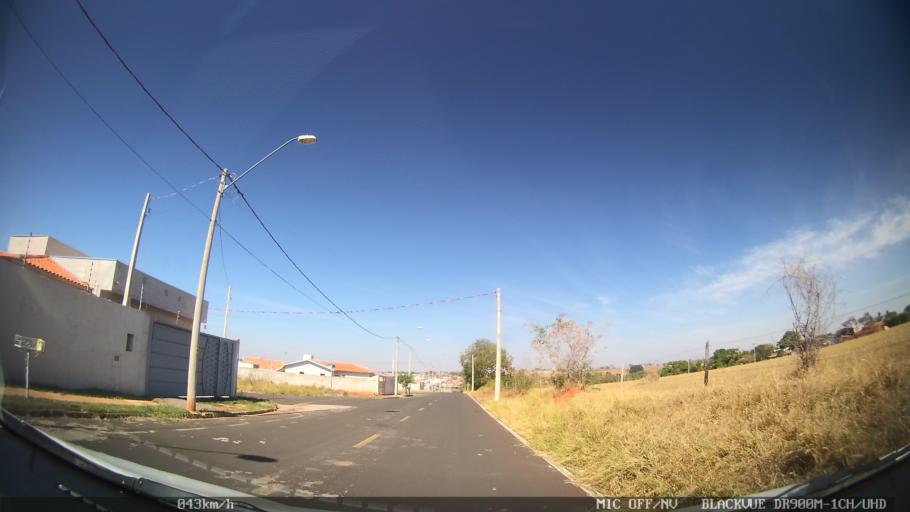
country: BR
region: Sao Paulo
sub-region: Sao Jose Do Rio Preto
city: Sao Jose do Rio Preto
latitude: -20.7579
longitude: -49.4238
